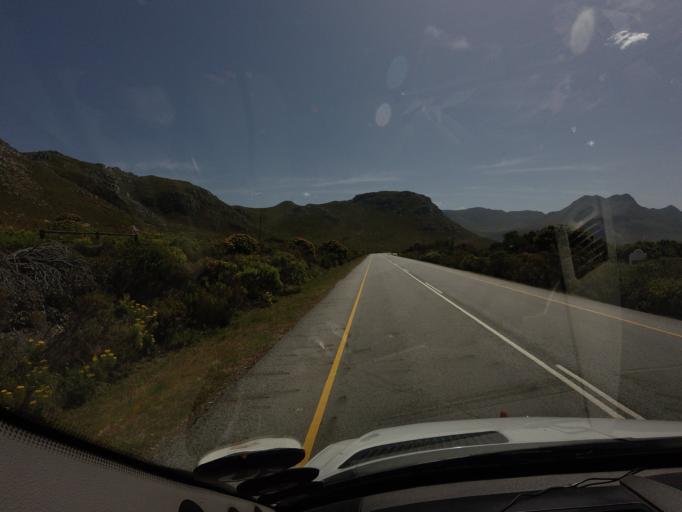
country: ZA
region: Western Cape
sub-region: Overberg District Municipality
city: Grabouw
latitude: -34.3493
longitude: 18.9753
